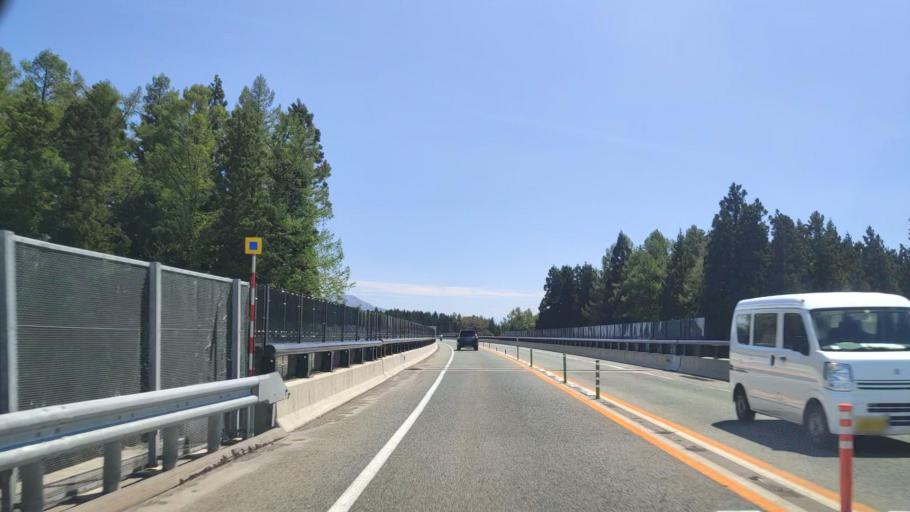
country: JP
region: Yamagata
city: Obanazawa
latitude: 38.6333
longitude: 140.3728
